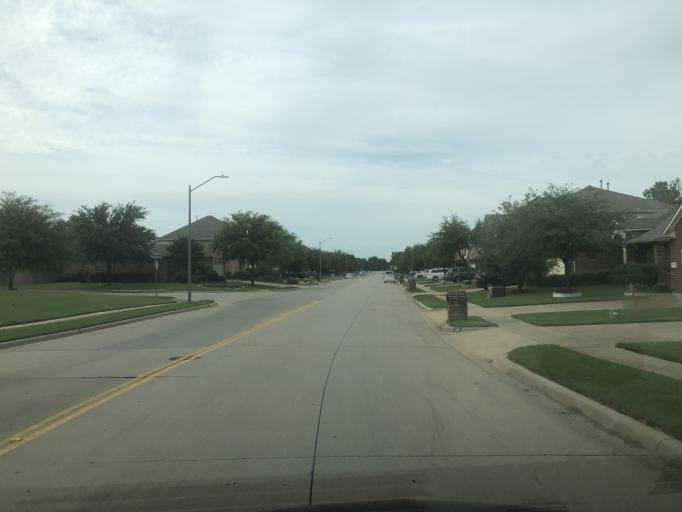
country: US
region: Texas
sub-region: Dallas County
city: Irving
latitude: 32.8024
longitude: -96.9921
